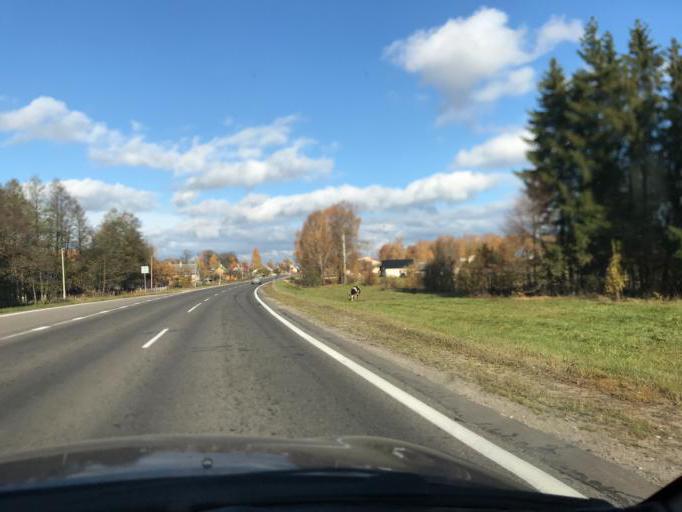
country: LT
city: Salcininkai
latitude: 54.2371
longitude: 25.3555
